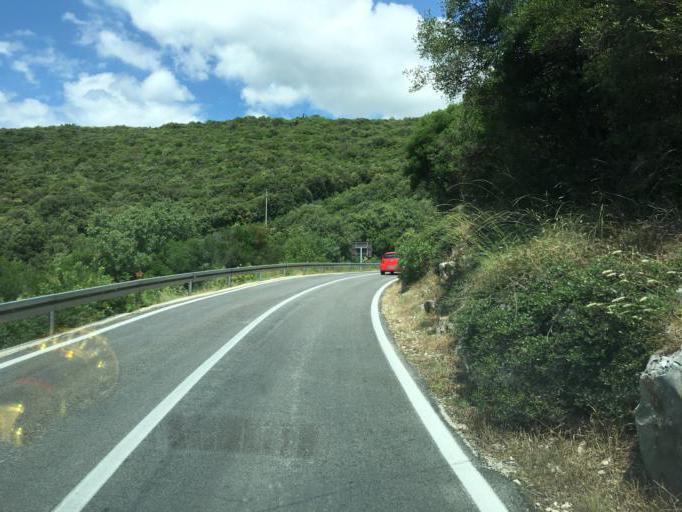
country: HR
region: Istarska
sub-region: Grad Rovinj
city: Rovinj
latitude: 45.1326
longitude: 13.7367
